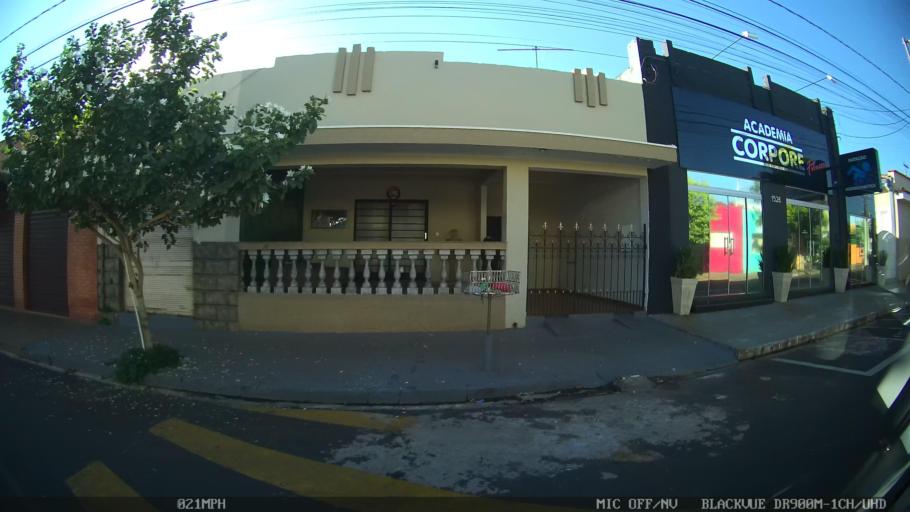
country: BR
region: Sao Paulo
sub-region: Olimpia
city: Olimpia
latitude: -20.7394
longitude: -48.9184
